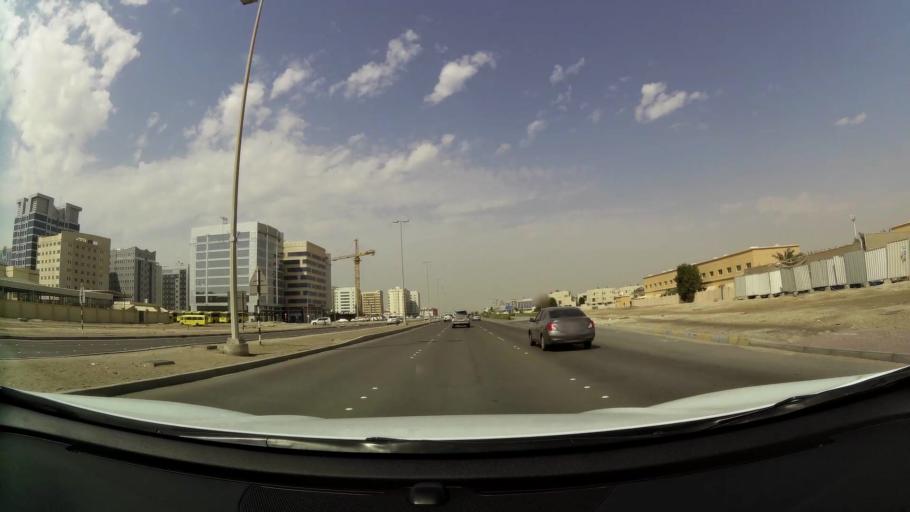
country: AE
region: Abu Dhabi
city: Abu Dhabi
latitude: 24.3394
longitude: 54.5385
